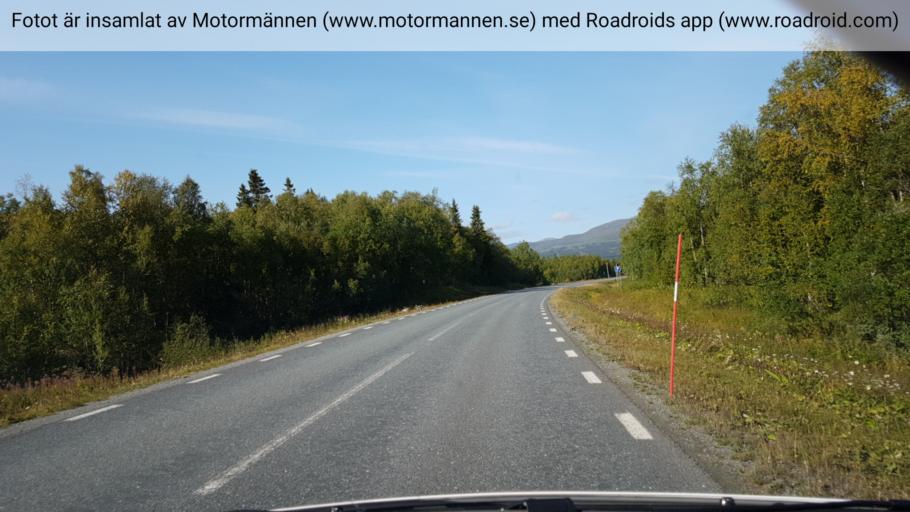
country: NO
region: Nordland
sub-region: Rana
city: Mo i Rana
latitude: 65.7707
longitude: 15.1127
